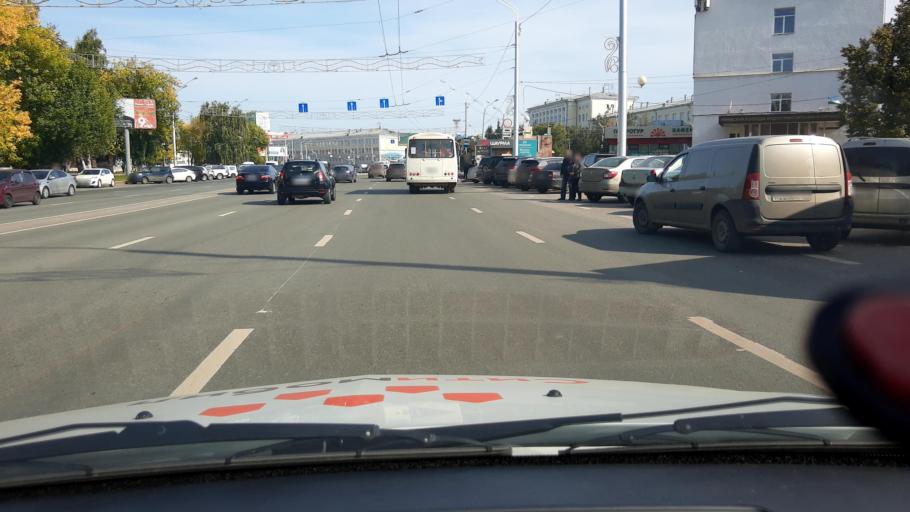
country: RU
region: Bashkortostan
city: Ufa
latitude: 54.7415
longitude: 55.9834
